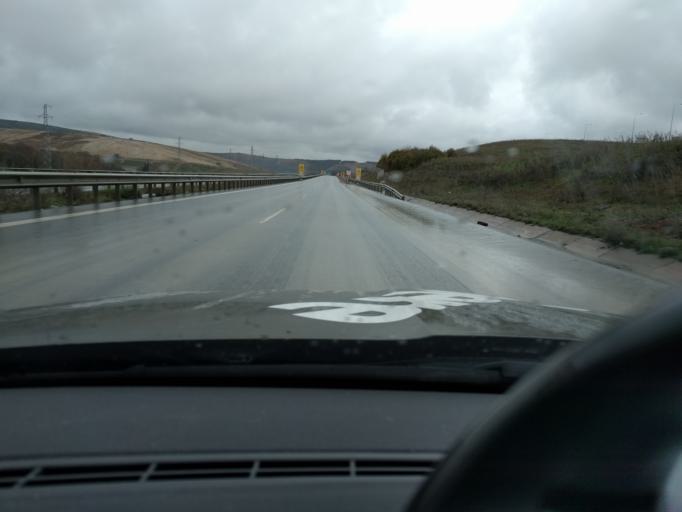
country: TR
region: Istanbul
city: Kemerburgaz
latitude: 41.2284
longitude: 28.8452
